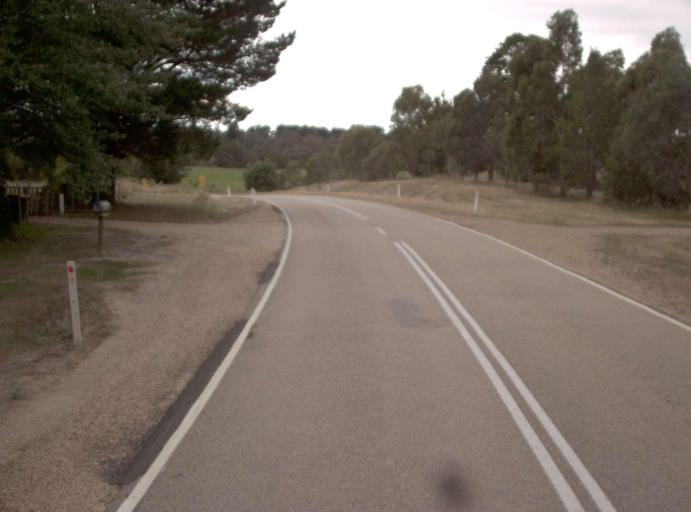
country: AU
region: Victoria
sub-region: Wellington
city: Sale
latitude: -38.0045
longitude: 147.2626
